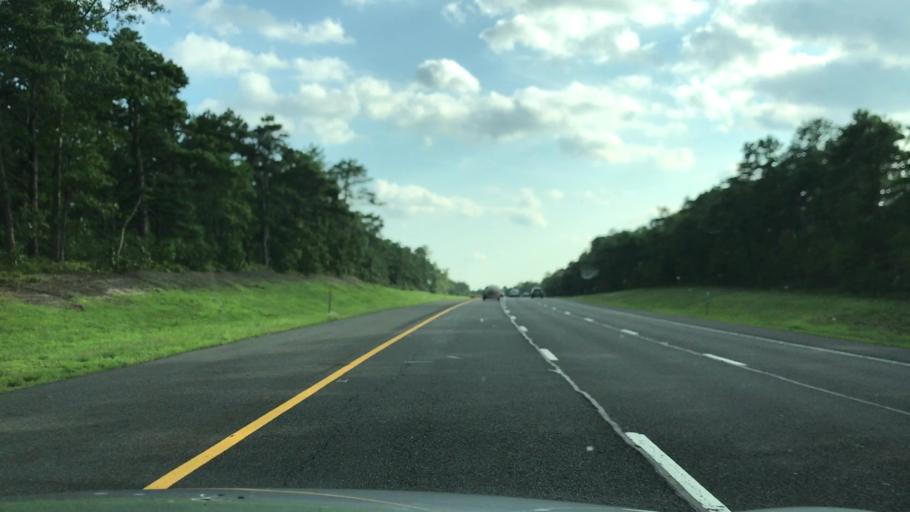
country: US
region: New Jersey
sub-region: Ocean County
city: Manahawkin
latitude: 39.6789
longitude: -74.3075
